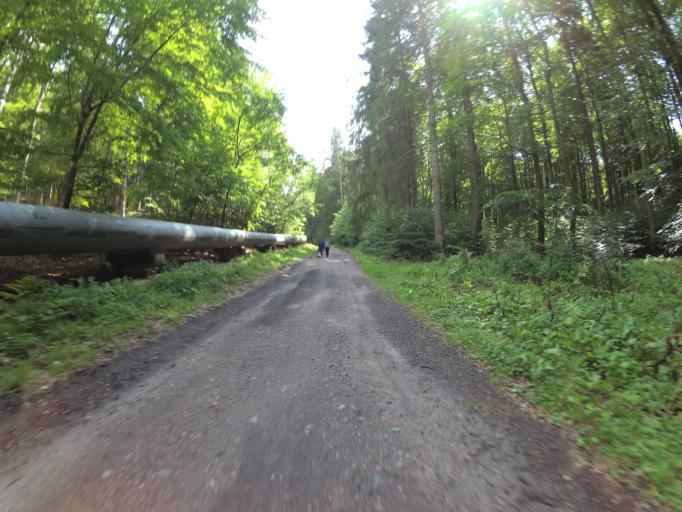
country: PL
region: Pomeranian Voivodeship
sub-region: Gdynia
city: Wielki Kack
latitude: 54.5105
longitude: 18.4860
